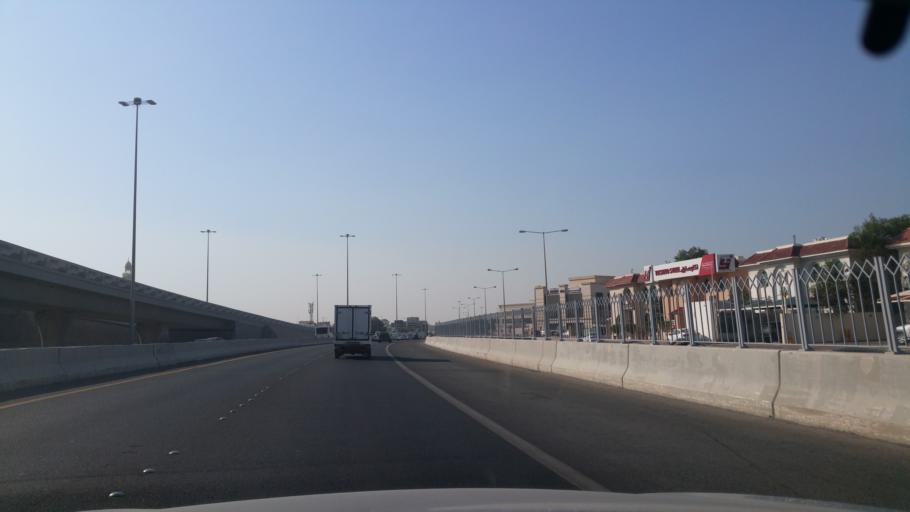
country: QA
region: Baladiyat ad Dawhah
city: Doha
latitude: 25.2550
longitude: 51.5071
